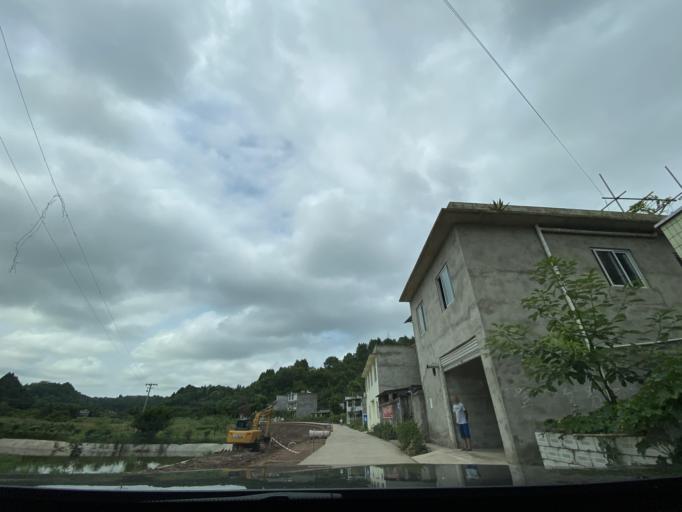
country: CN
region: Sichuan
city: Jiancheng
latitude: 30.4046
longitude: 104.5745
